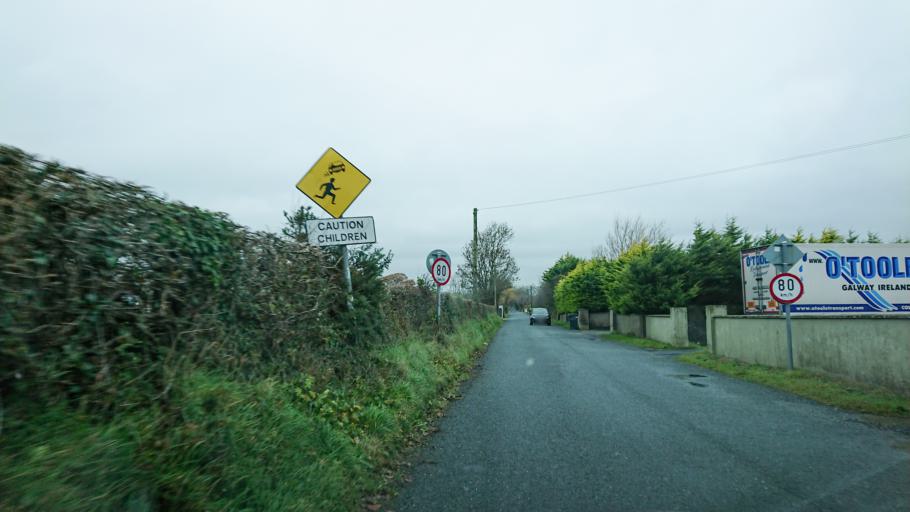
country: IE
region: Munster
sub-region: Waterford
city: Waterford
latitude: 52.2385
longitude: -7.1792
